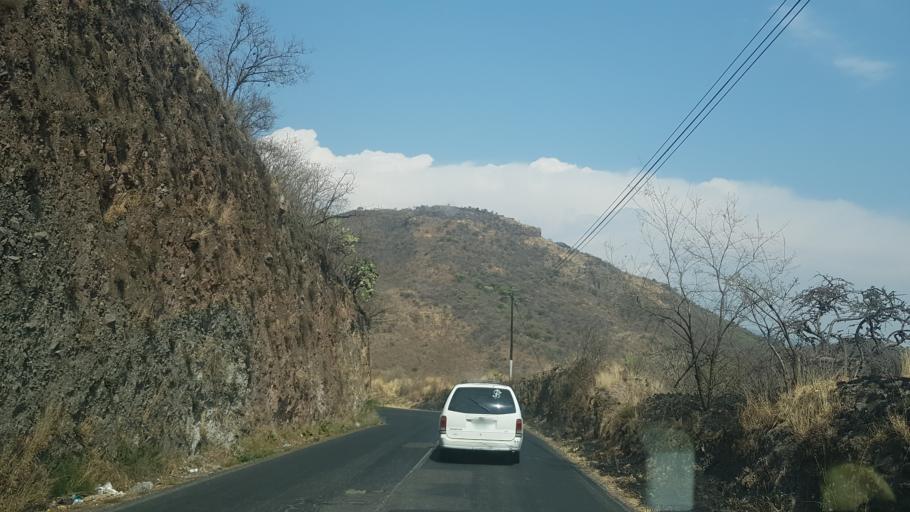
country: MX
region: Puebla
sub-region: Tianguismanalco
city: San Martin Tlapala
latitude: 18.9469
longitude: -98.4571
